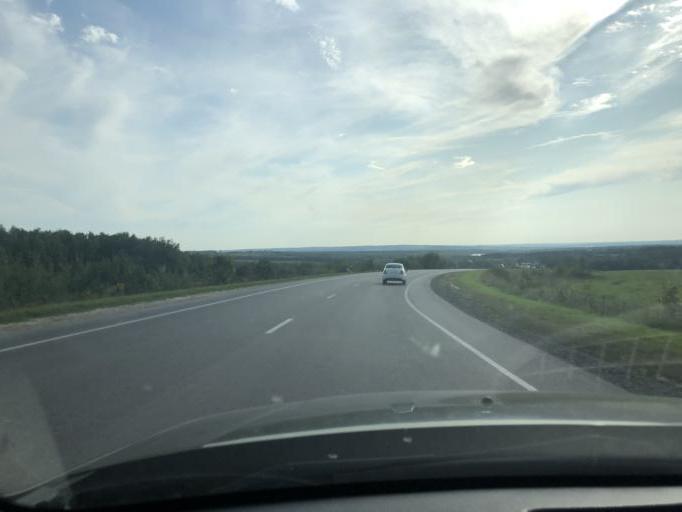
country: RU
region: Tula
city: Krapivna
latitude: 54.1217
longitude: 37.2396
